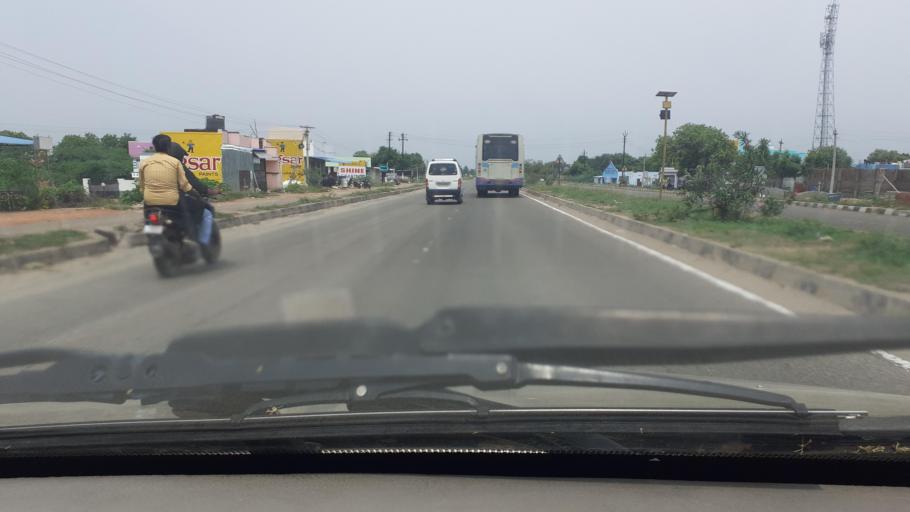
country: IN
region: Tamil Nadu
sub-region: Thoothukkudi
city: Srivaikuntam
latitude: 8.7370
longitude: 77.9193
